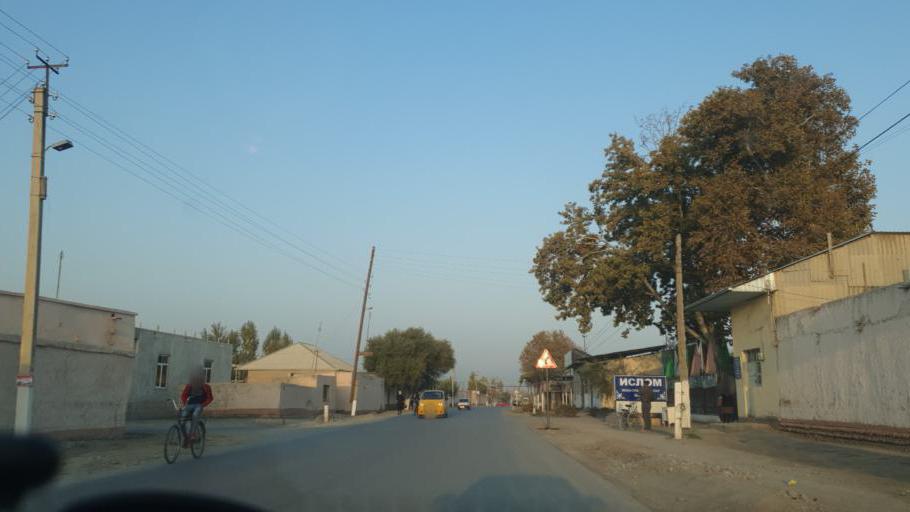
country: UZ
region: Fergana
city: Yaypan
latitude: 40.3763
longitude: 70.7906
